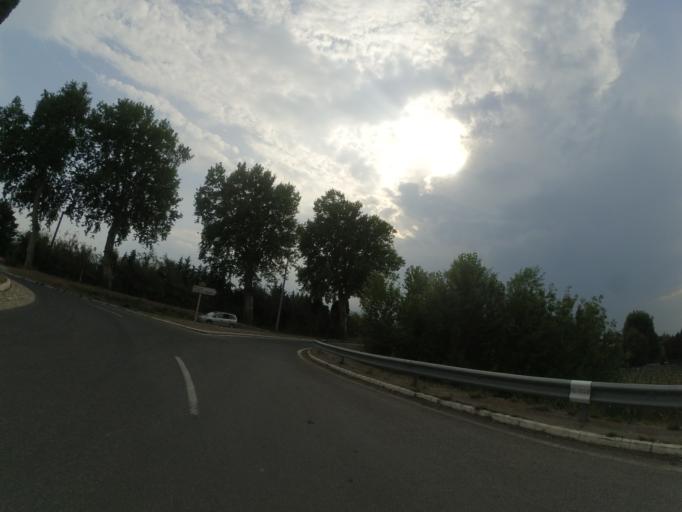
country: FR
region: Languedoc-Roussillon
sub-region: Departement des Pyrenees-Orientales
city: Corneilla-la-Riviere
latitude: 42.6847
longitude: 2.7289
